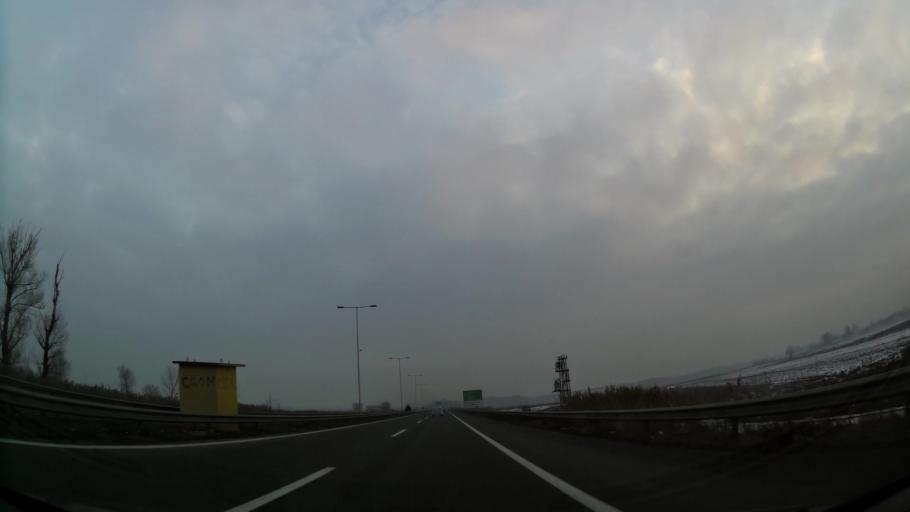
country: MK
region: Aracinovo
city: Arachinovo
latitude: 42.0039
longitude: 21.5344
